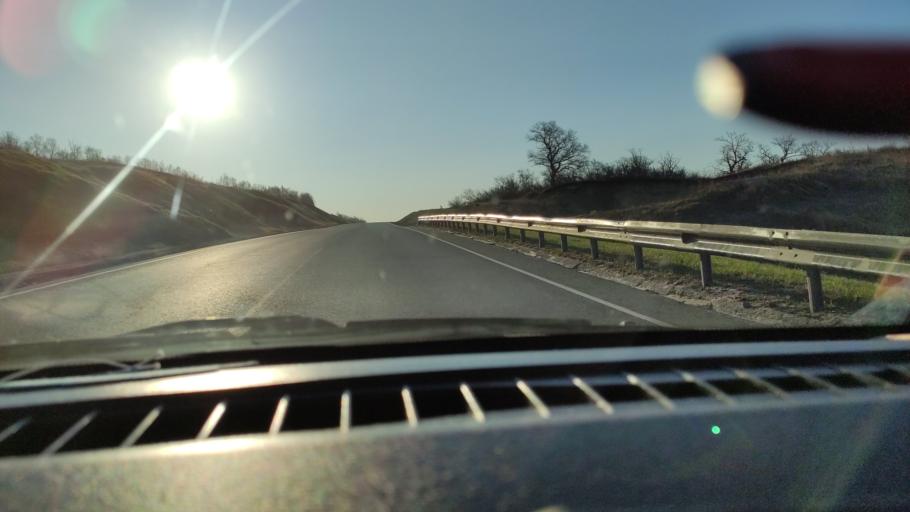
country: RU
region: Saratov
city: Tersa
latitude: 52.1035
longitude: 47.4926
